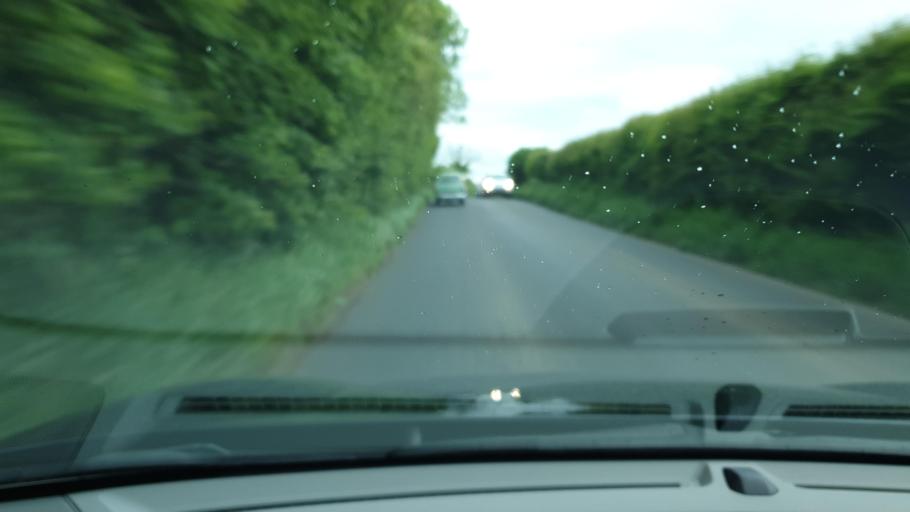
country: IE
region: Leinster
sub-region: An Mhi
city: Ashbourne
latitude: 53.5355
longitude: -6.4059
